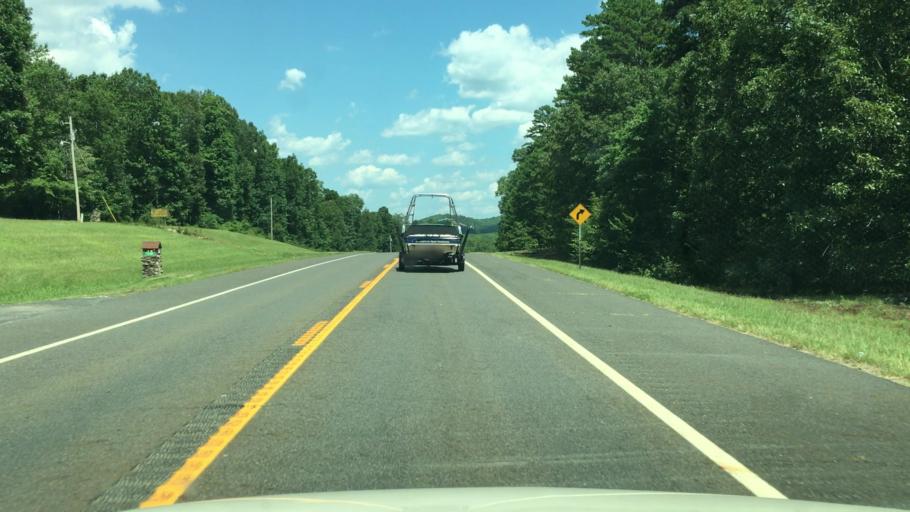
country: US
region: Arkansas
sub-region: Garland County
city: Lake Hamilton
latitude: 34.3778
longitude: -93.1537
